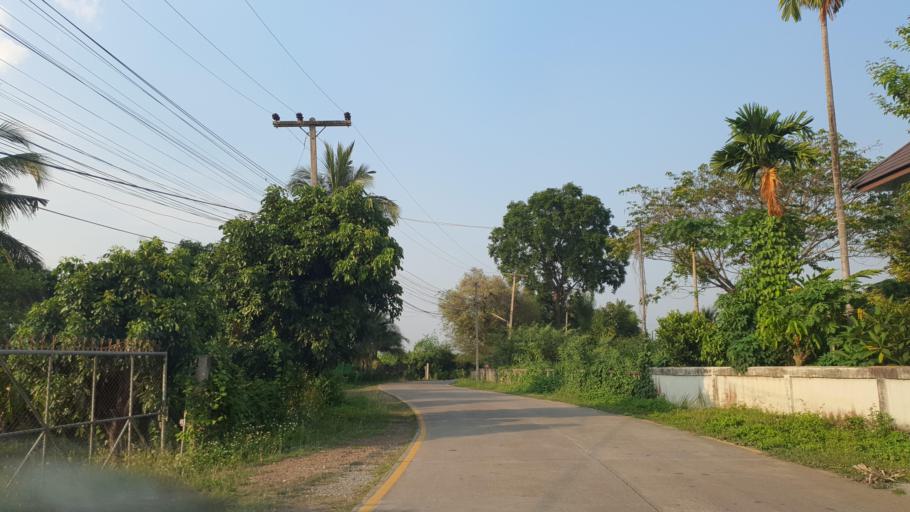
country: TH
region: Chiang Mai
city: San Pa Tong
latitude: 18.6364
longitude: 98.8679
